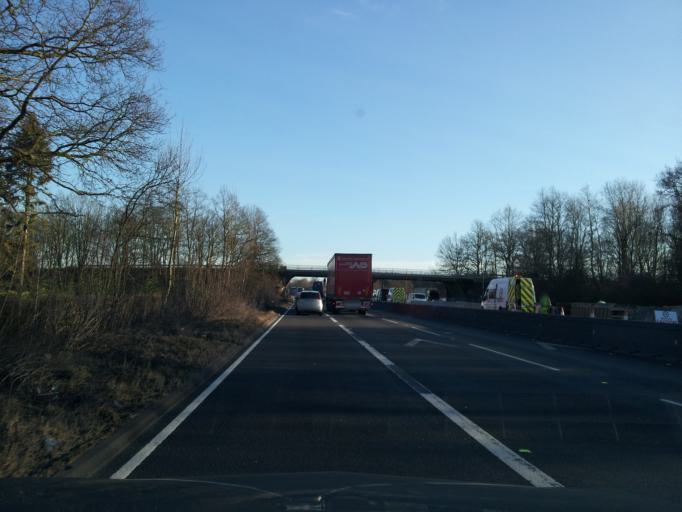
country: GB
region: England
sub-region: Northamptonshire
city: Long Buckby
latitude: 52.2535
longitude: -1.0749
